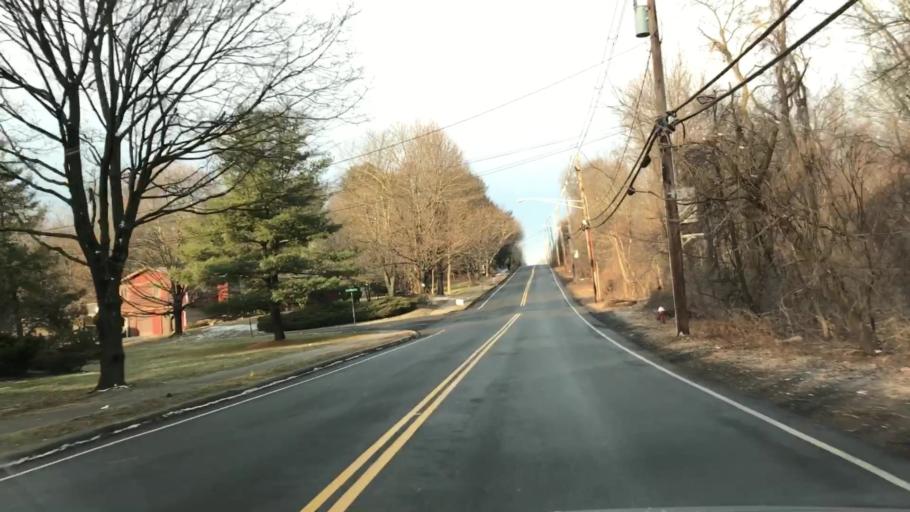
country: US
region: New York
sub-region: Rockland County
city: Kaser
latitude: 41.1356
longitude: -74.0680
